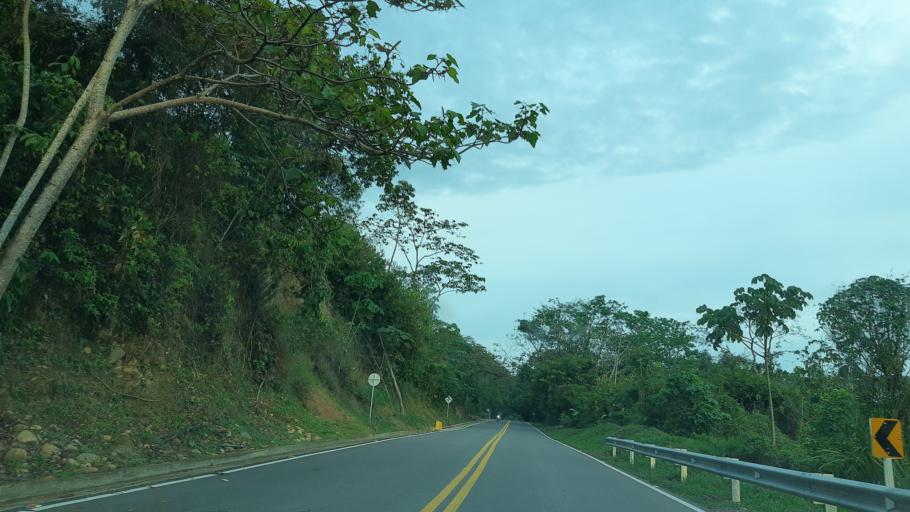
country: CO
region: Casanare
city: Sabanalarga
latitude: 4.7722
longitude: -73.0468
